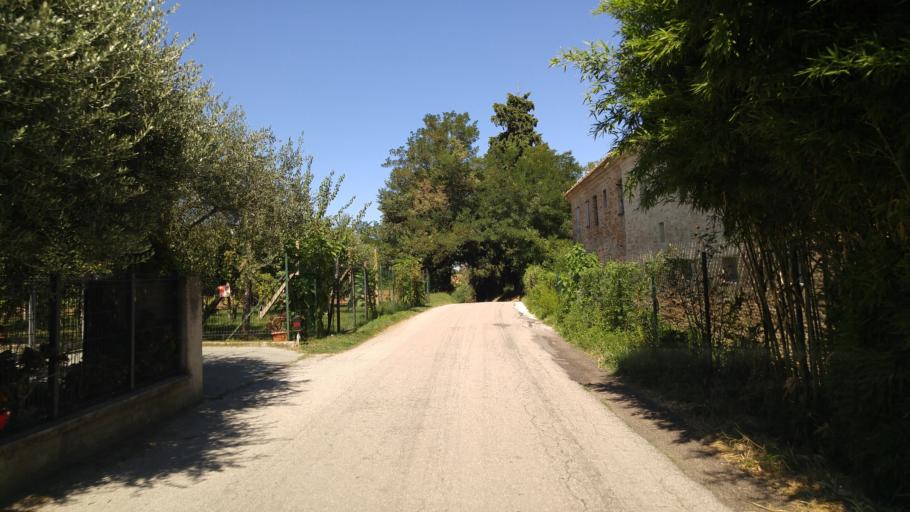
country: IT
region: The Marches
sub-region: Provincia di Pesaro e Urbino
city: Cuccurano
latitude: 43.7757
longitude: 12.9617
